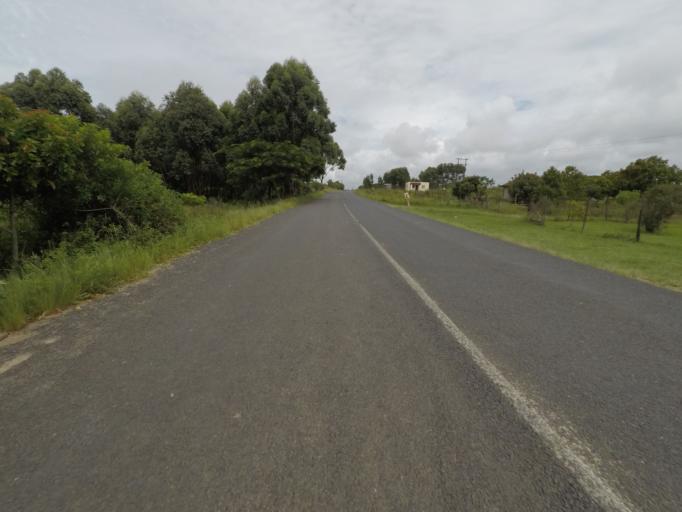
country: ZA
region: KwaZulu-Natal
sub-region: uThungulu District Municipality
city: eSikhawini
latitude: -28.9122
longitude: 31.8618
